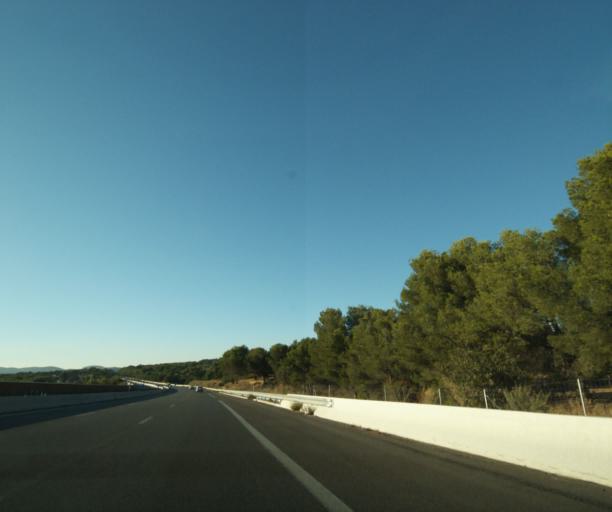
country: FR
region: Provence-Alpes-Cote d'Azur
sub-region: Departement des Bouches-du-Rhone
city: Ceyreste
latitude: 43.1937
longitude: 5.6511
